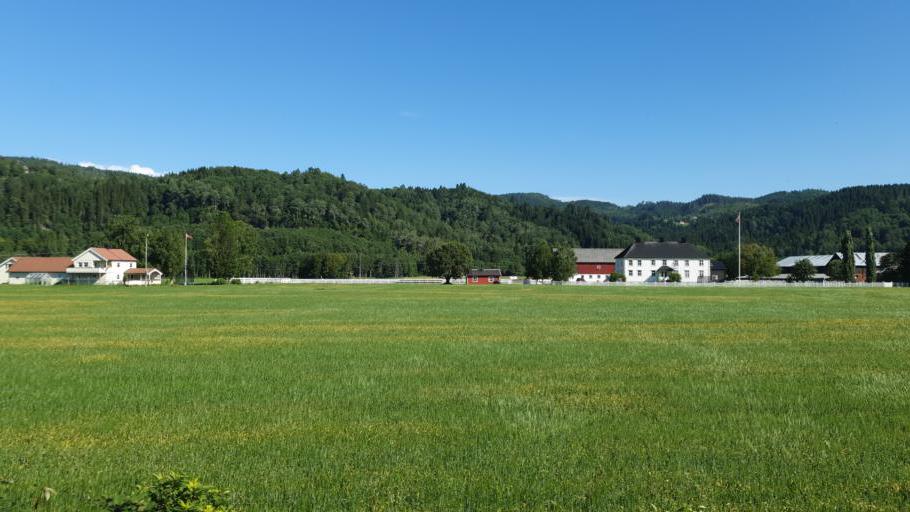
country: NO
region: Sor-Trondelag
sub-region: Orkdal
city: Orkanger
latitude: 63.2043
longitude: 9.7838
